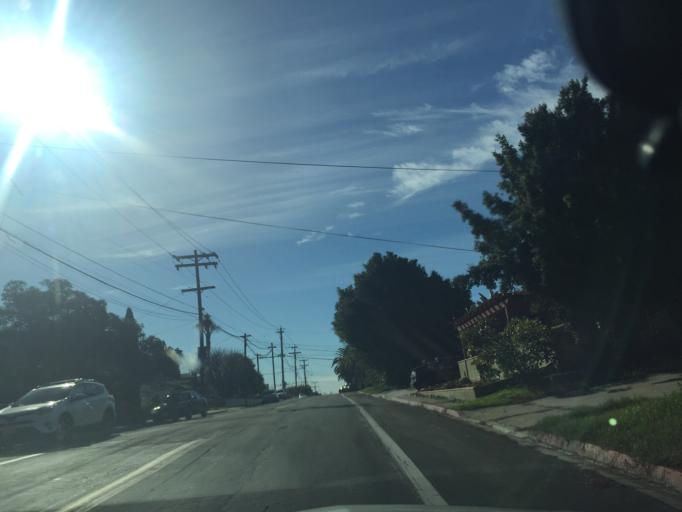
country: US
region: California
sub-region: San Diego County
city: Lemon Grove
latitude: 32.7645
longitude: -117.0794
